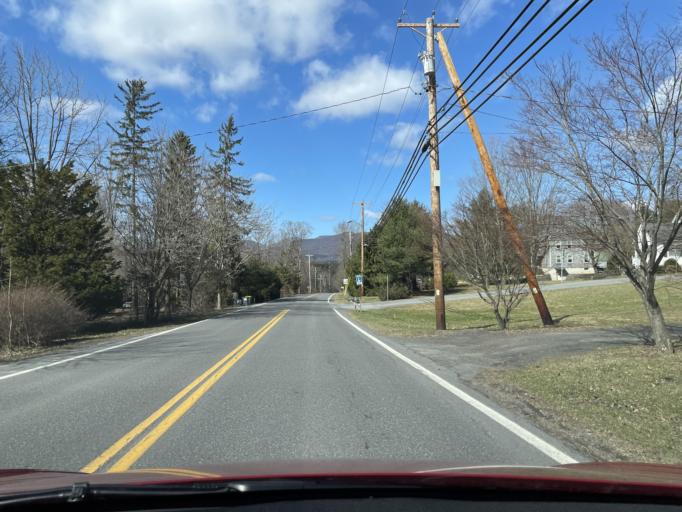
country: US
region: New York
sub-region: Ulster County
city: West Hurley
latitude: 41.9995
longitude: -74.1051
